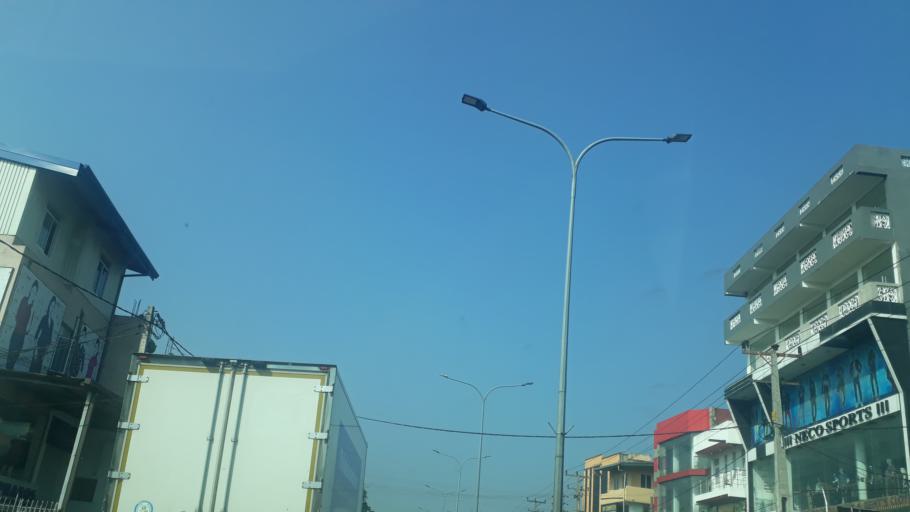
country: LK
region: Western
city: Kelaniya
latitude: 6.9687
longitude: 79.9113
